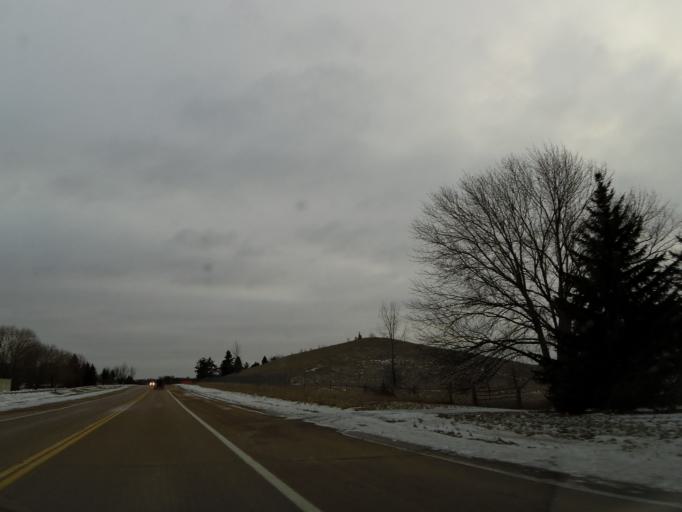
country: US
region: Minnesota
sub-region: Carver County
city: Carver
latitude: 44.7575
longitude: -93.6427
